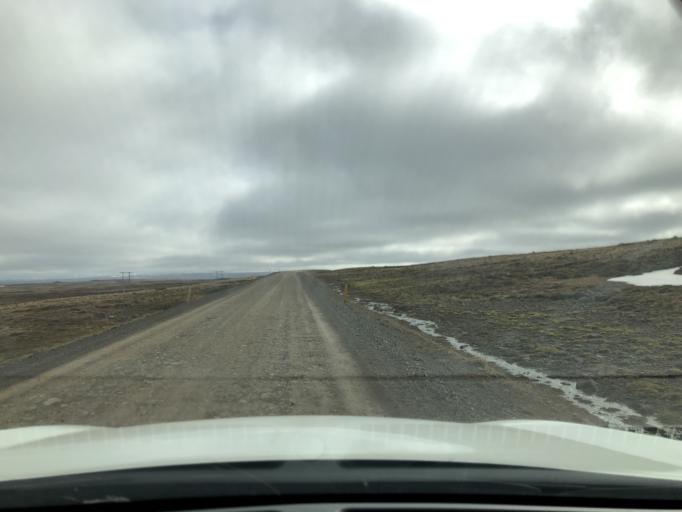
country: IS
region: West
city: Borgarnes
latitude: 65.2066
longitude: -21.3230
